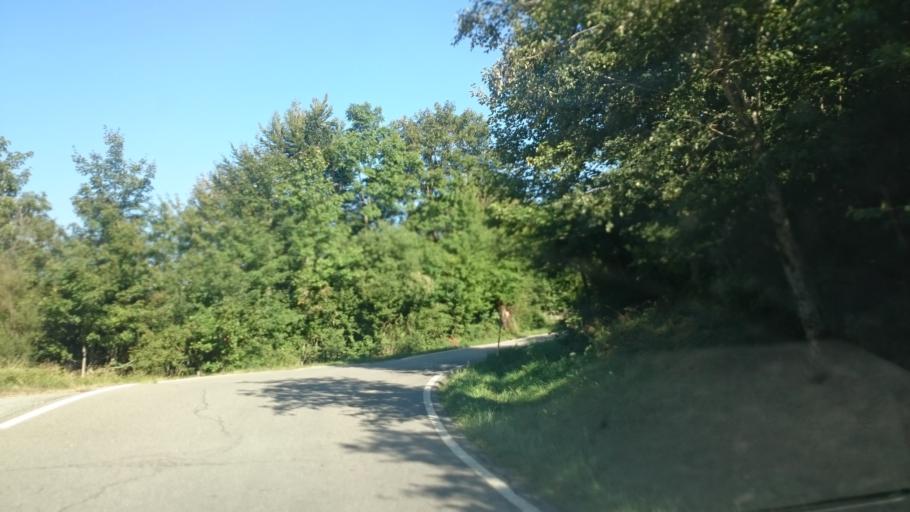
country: IT
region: Emilia-Romagna
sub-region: Provincia di Reggio Emilia
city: Villa Minozzo
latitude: 44.2998
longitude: 10.4357
